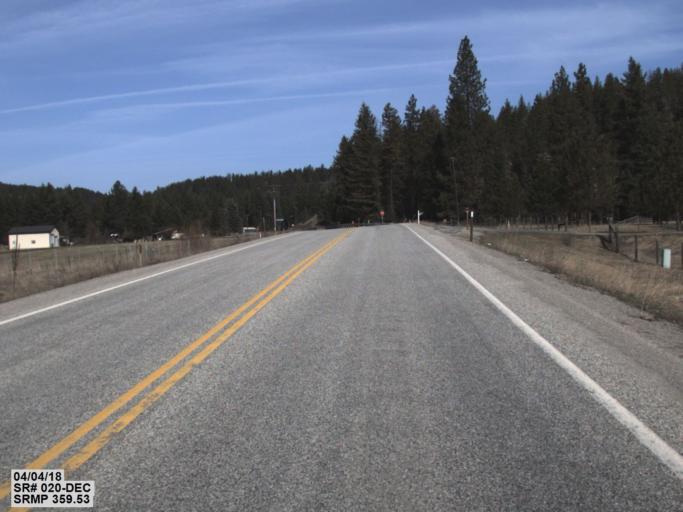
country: US
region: Washington
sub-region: Stevens County
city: Colville
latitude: 48.5222
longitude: -117.8141
